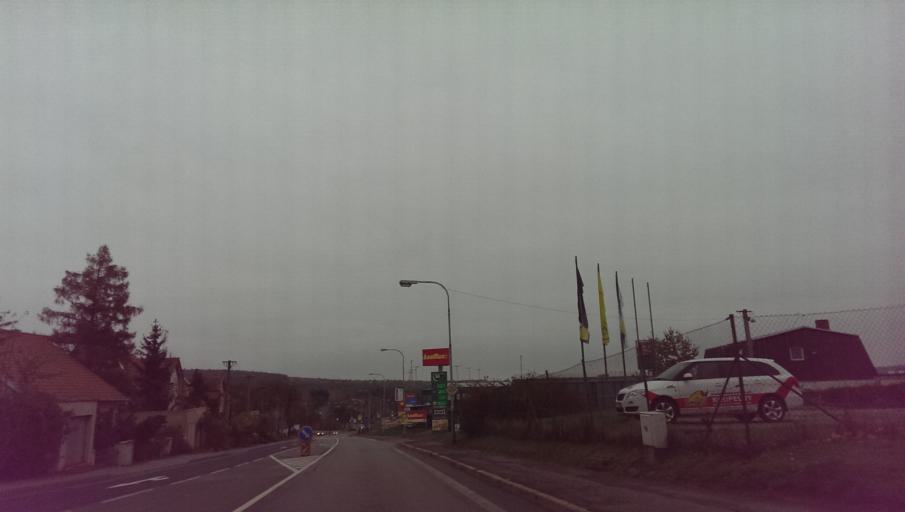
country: CZ
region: South Moravian
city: Dobsice
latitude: 48.8570
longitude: 16.0696
